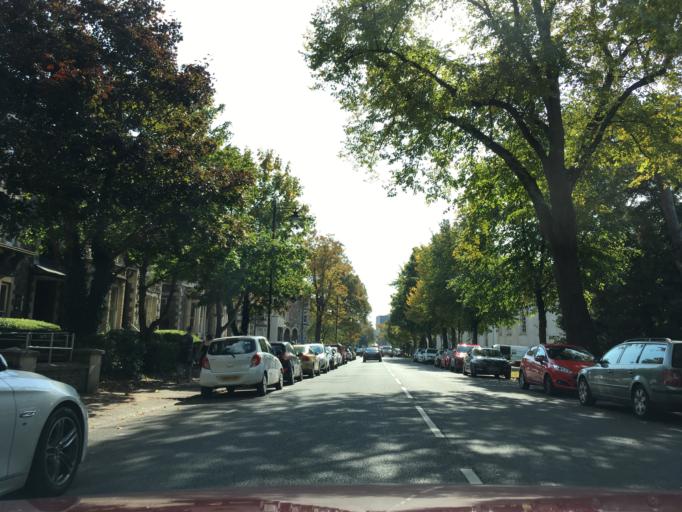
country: GB
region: Wales
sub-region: Cardiff
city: Cardiff
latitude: 51.4873
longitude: -3.1774
